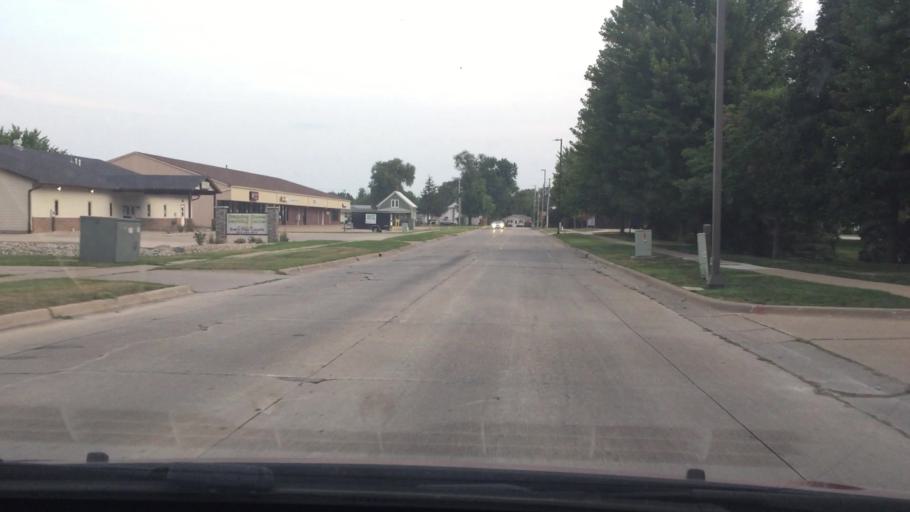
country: US
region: Iowa
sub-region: Muscatine County
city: Muscatine
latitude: 41.4491
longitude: -91.0355
